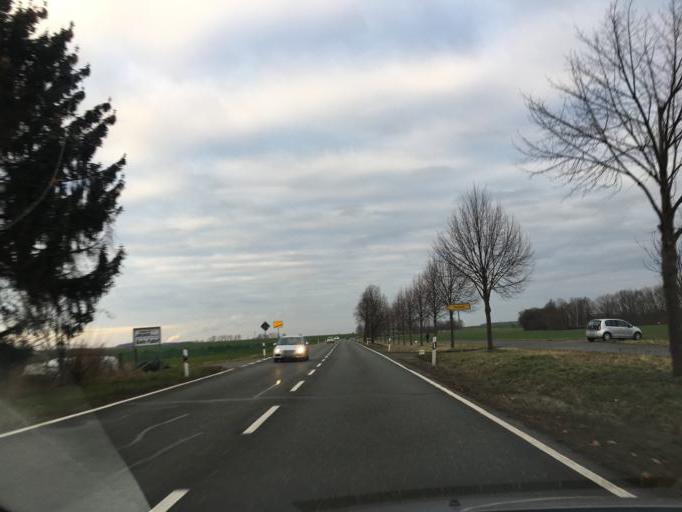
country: DE
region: Thuringia
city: Fockendorf
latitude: 51.0288
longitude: 12.4582
